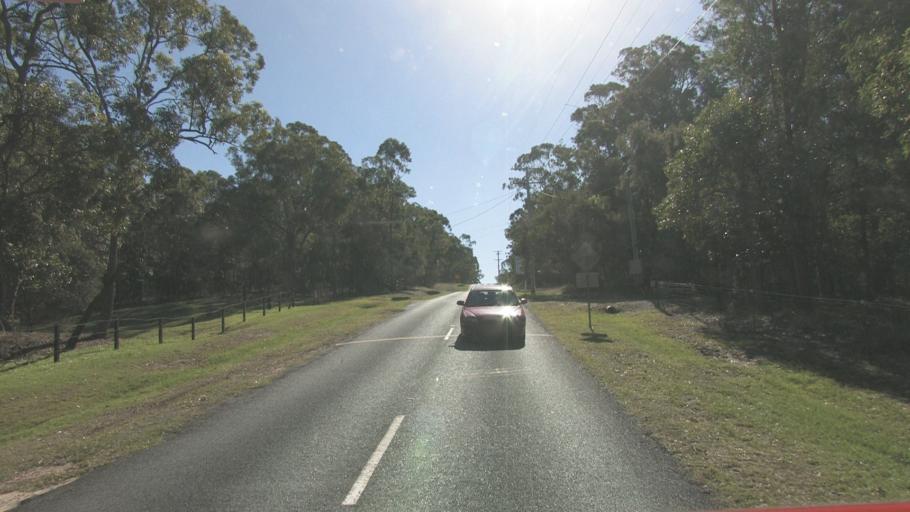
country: AU
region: Queensland
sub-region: Logan
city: Springwood
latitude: -27.6002
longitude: 153.1664
